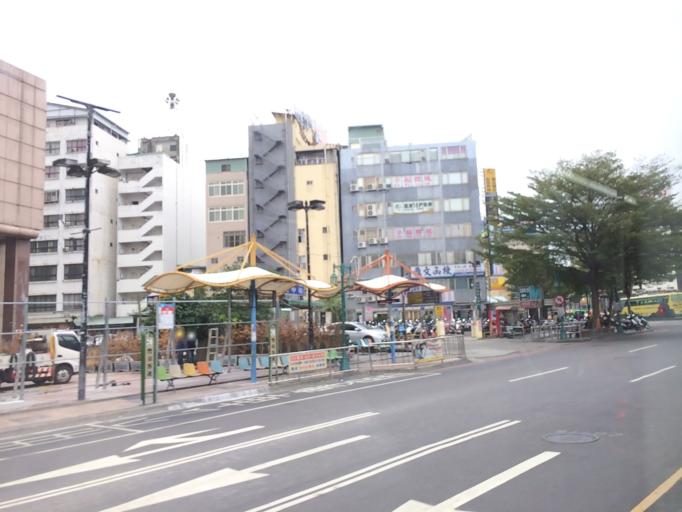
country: TW
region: Taiwan
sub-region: Taichung City
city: Taichung
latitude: 24.1364
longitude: 120.6835
